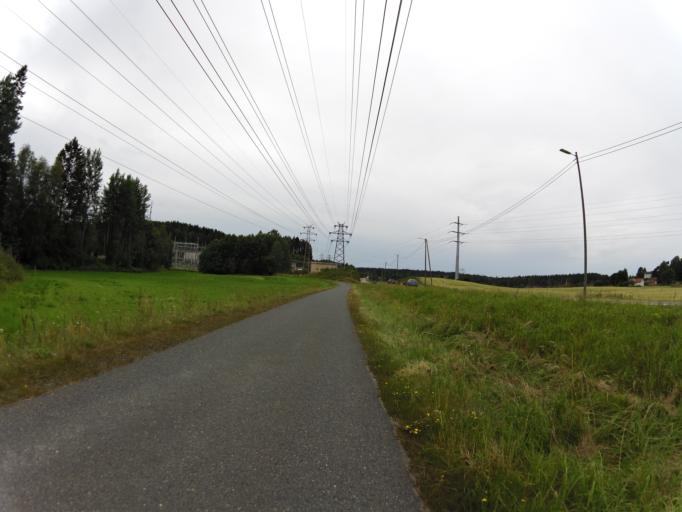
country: NO
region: Akershus
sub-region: Vestby
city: Vestby
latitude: 59.5187
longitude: 10.7425
